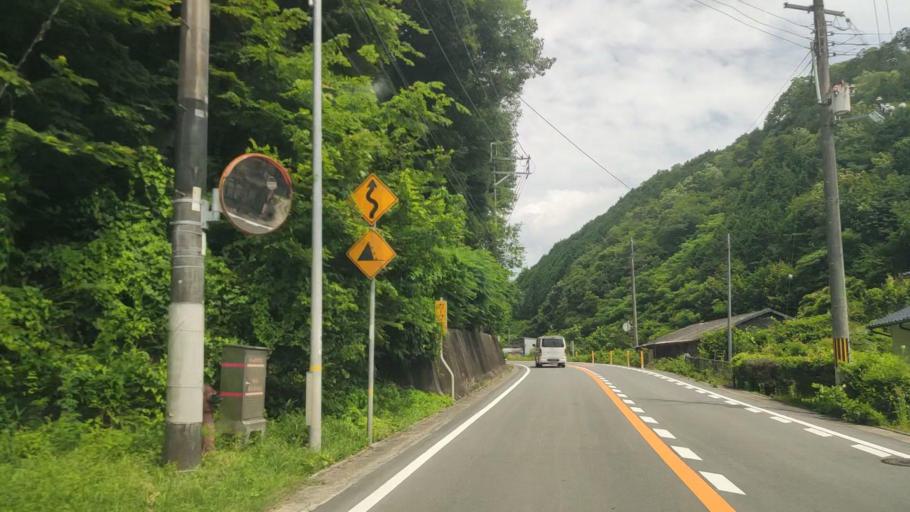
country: JP
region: Hyogo
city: Yamazakicho-nakabirose
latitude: 34.9927
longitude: 134.3996
